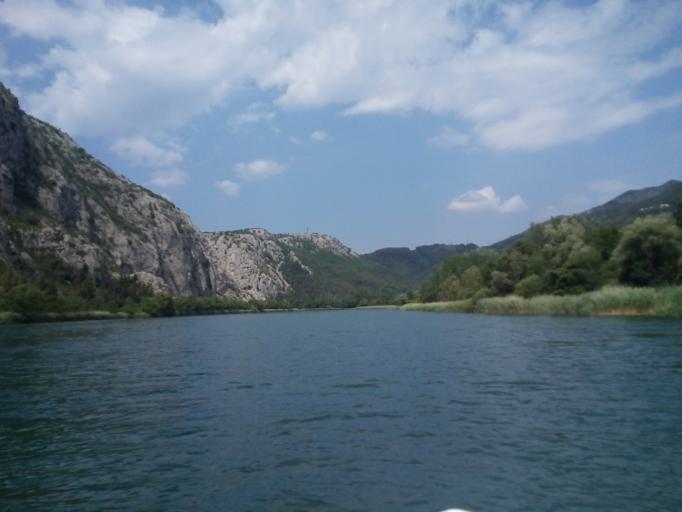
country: HR
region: Splitsko-Dalmatinska
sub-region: Grad Omis
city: Omis
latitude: 43.4502
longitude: 16.7104
